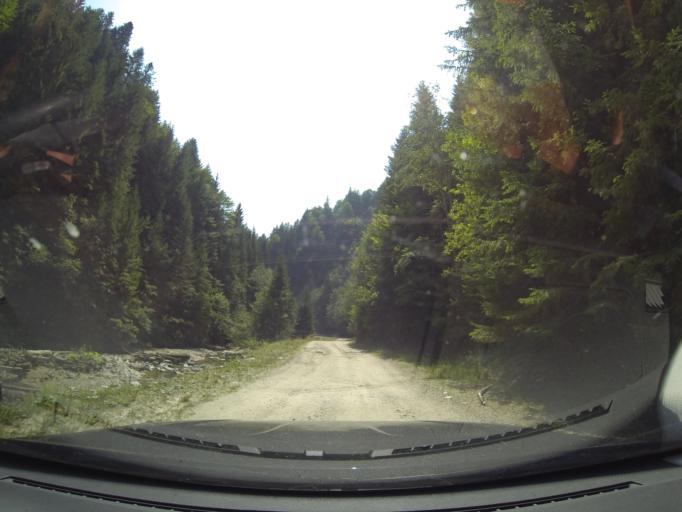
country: RO
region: Arges
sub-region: Comuna Arefu
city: Arefu
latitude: 45.4678
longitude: 24.6344
